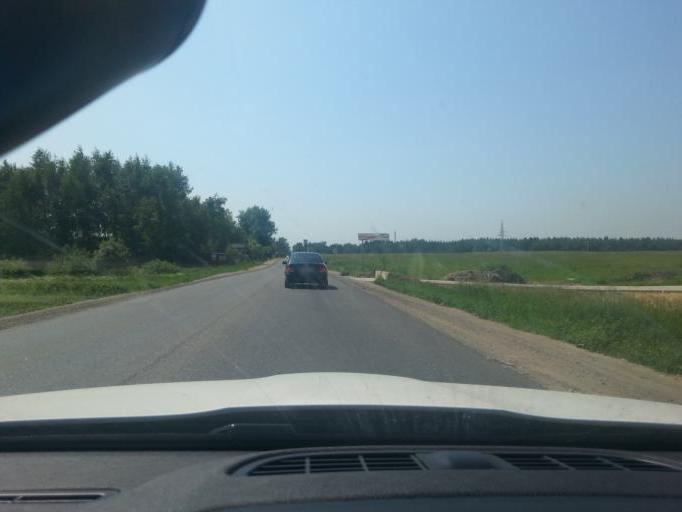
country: RU
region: Moskovskaya
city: Zheleznodorozhnyy
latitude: 55.7250
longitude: 37.9765
